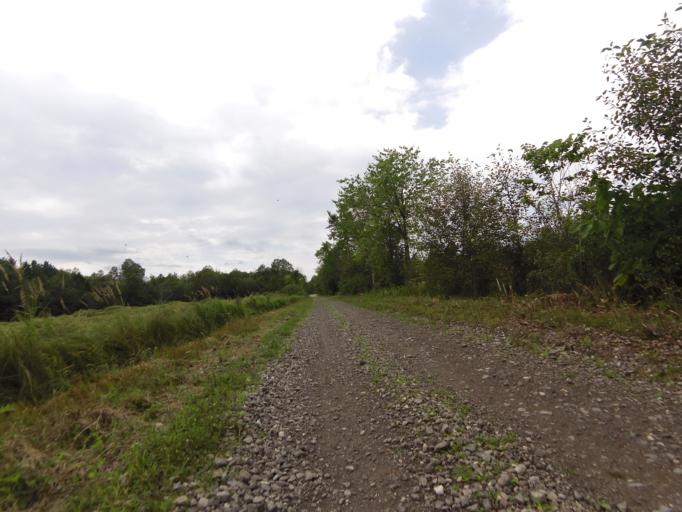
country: CA
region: Ontario
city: Perth
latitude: 44.8197
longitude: -76.5862
